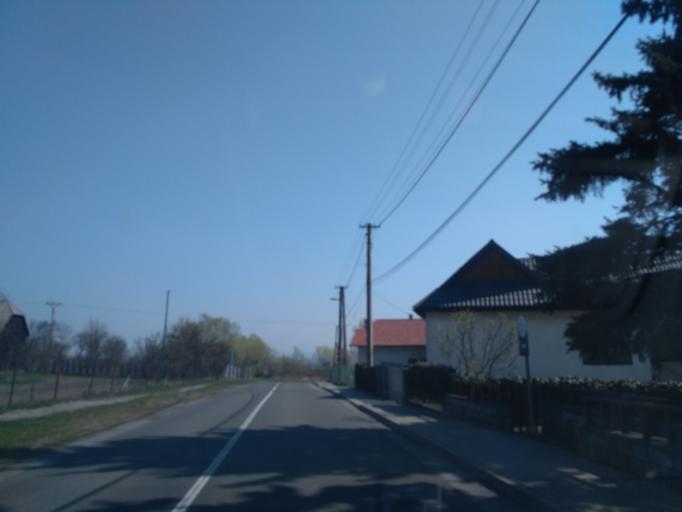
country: SK
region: Kosicky
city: Secovce
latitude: 48.7592
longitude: 21.6421
